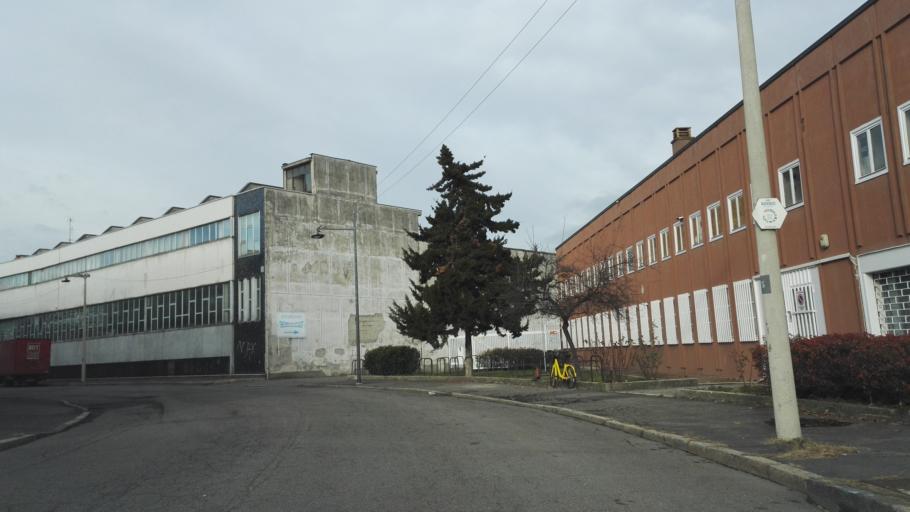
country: IT
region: Lombardy
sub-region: Citta metropolitana di Milano
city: Linate
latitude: 45.4508
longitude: 9.2428
